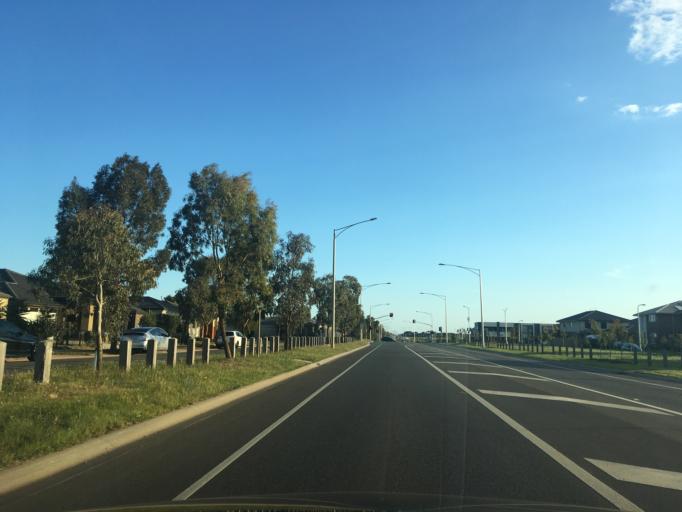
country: AU
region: Victoria
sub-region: Wyndham
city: Hoppers Crossing
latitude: -37.8907
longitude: 144.7178
